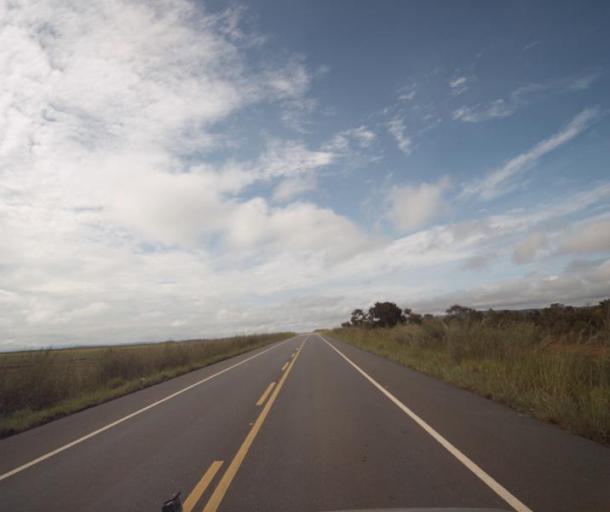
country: BR
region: Goias
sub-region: Barro Alto
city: Barro Alto
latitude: -15.2900
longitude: -48.6780
